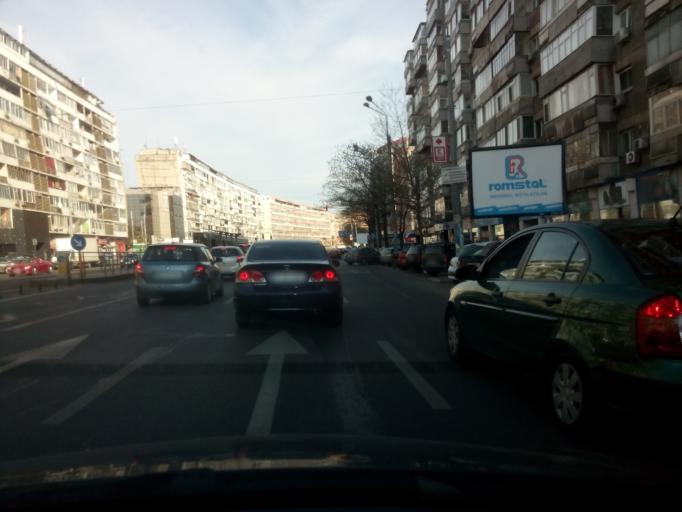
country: RO
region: Bucuresti
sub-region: Municipiul Bucuresti
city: Bucharest
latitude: 44.4523
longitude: 26.1183
